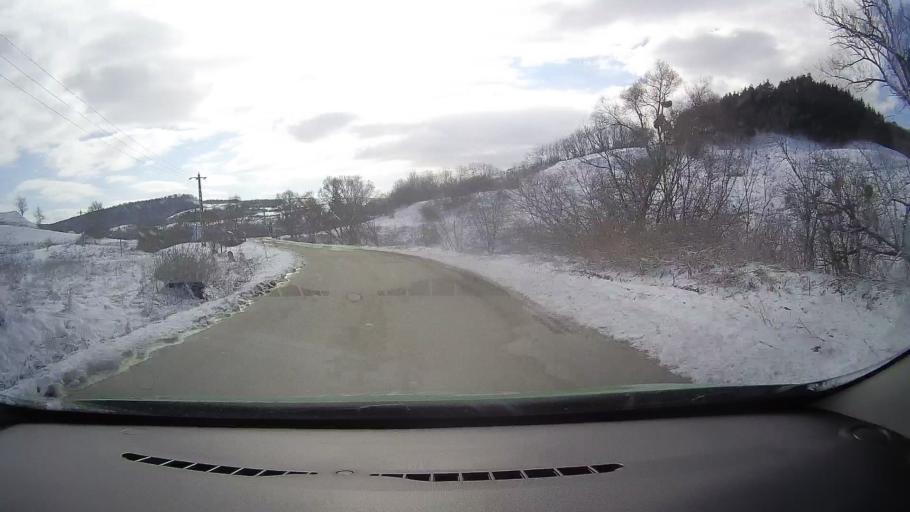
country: RO
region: Sibiu
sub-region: Comuna Mihaileni
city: Mihaileni
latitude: 46.0133
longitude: 24.3754
